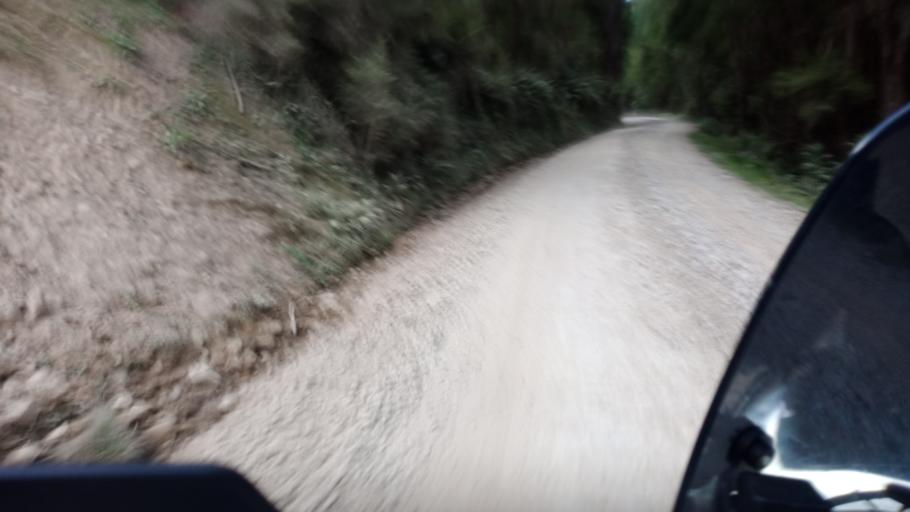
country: NZ
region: Gisborne
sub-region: Gisborne District
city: Gisborne
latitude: -38.4708
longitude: 177.9766
